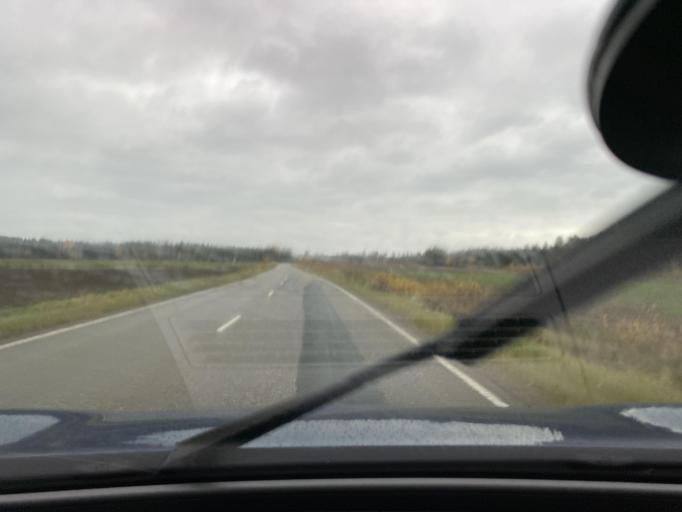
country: FI
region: Satakunta
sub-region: Rauma
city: Saekylae
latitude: 61.0411
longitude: 22.4049
